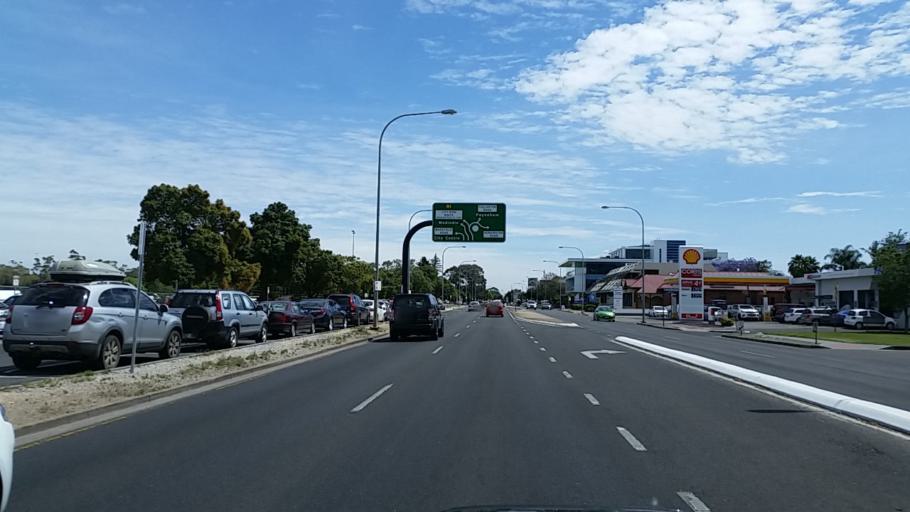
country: AU
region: South Australia
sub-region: Unley
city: Fullarton
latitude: -34.9316
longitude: 138.6239
